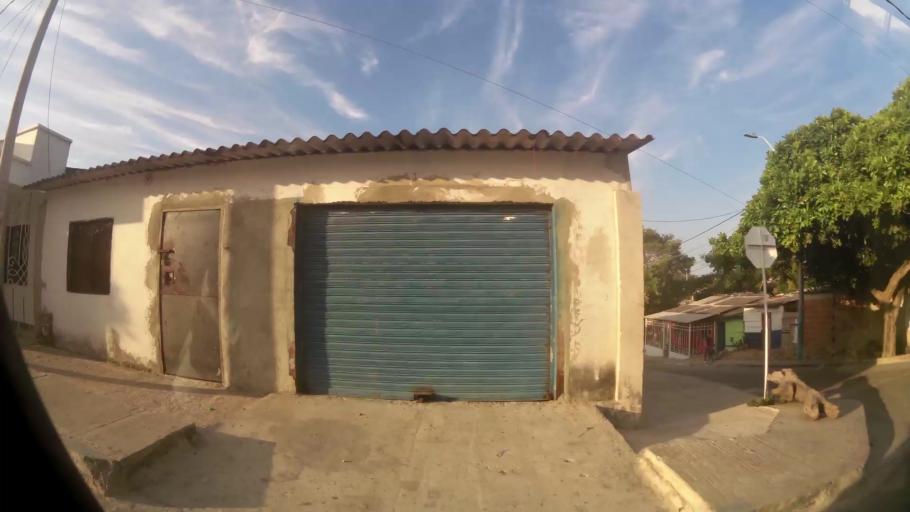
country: CO
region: Atlantico
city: Barranquilla
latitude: 10.9566
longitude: -74.8226
